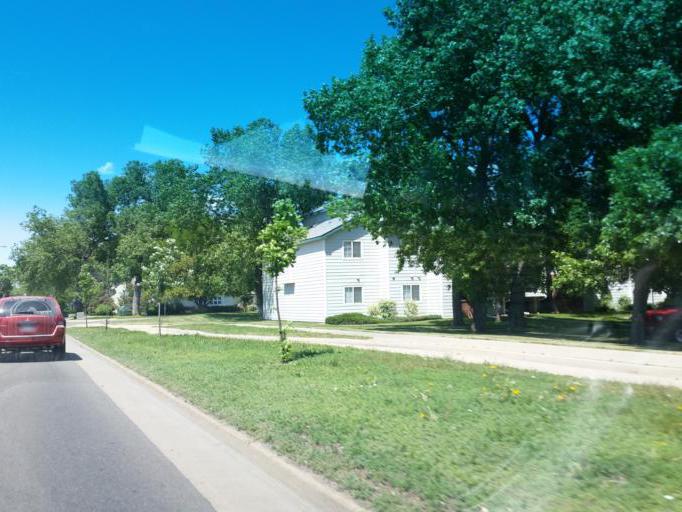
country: US
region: Colorado
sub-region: Larimer County
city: Fort Collins
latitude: 40.5387
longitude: -105.0961
